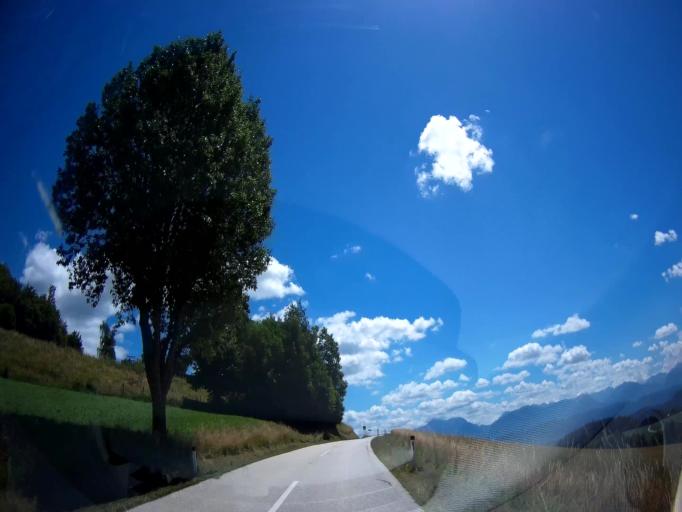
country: AT
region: Carinthia
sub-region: Politischer Bezirk Sankt Veit an der Glan
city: St. Georgen am Laengsee
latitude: 46.7206
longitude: 14.4220
